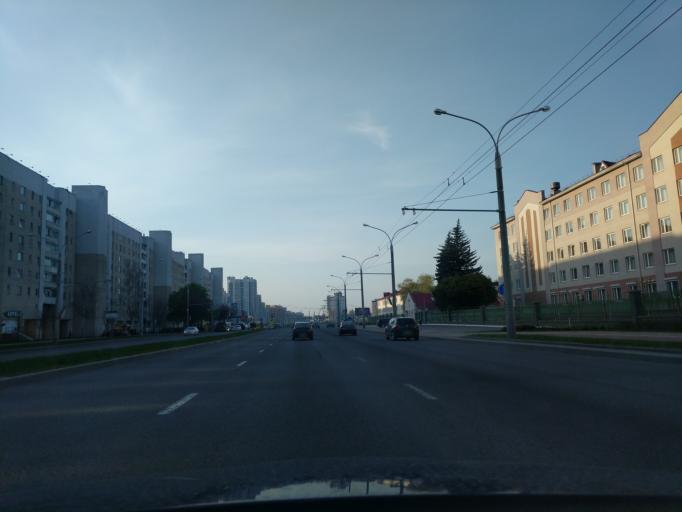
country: BY
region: Minsk
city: Minsk
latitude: 53.8673
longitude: 27.5706
